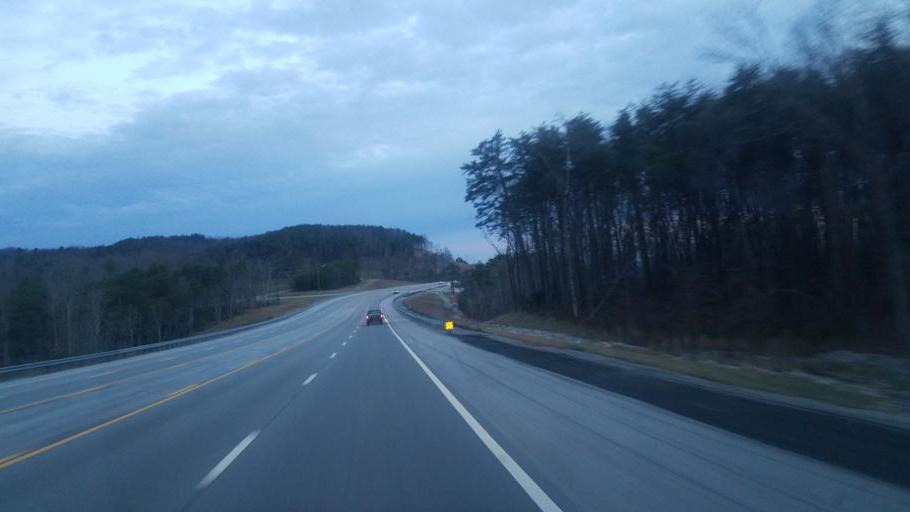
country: US
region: Tennessee
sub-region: Van Buren County
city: Spencer
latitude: 35.7668
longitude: -85.4626
